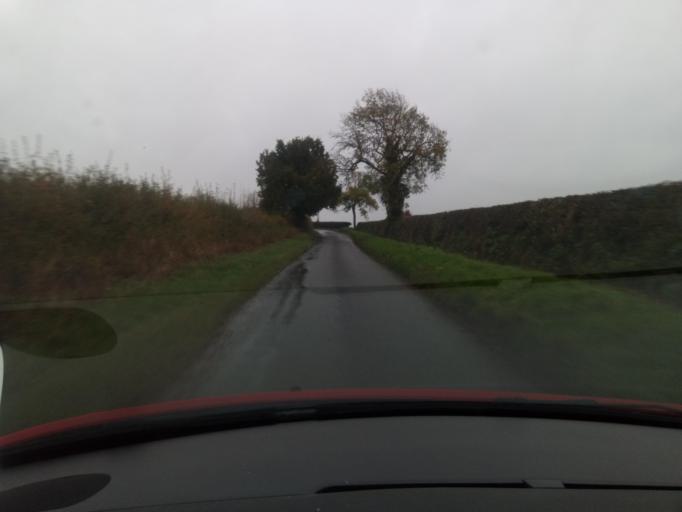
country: GB
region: England
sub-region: Derbyshire
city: Borrowash
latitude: 52.8652
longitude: -1.4011
